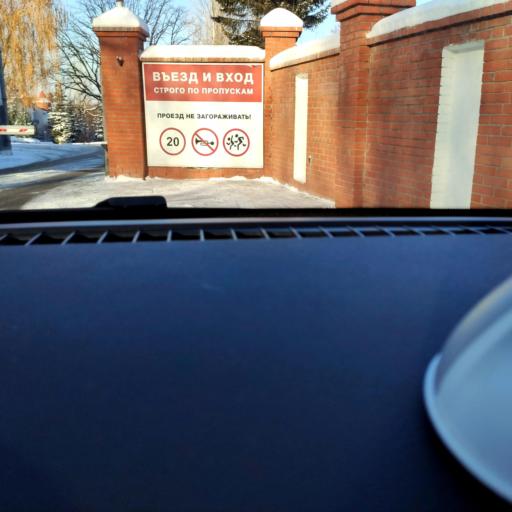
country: RU
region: Samara
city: Samara
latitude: 53.2764
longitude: 50.1913
